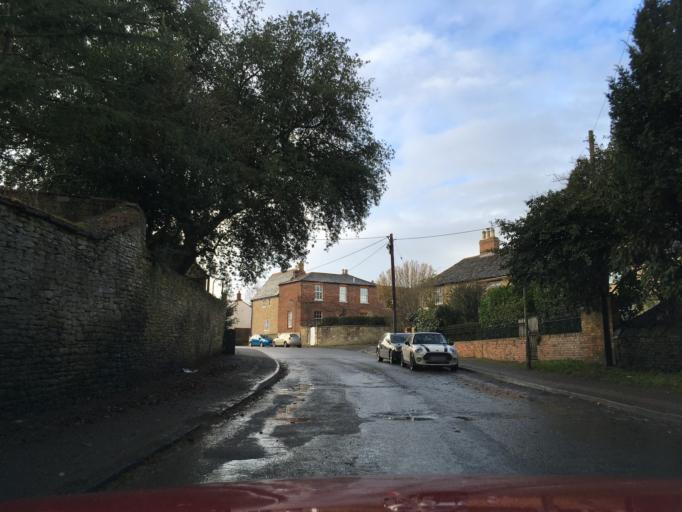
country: GB
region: England
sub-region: Oxfordshire
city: Eynsham
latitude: 51.7800
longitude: -1.3709
